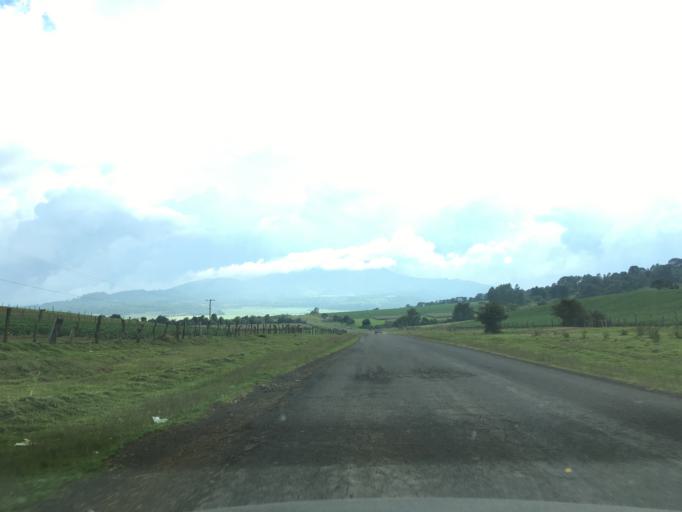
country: MX
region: Michoacan
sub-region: Nahuatzen
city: Sevina
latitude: 19.6364
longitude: -101.8342
